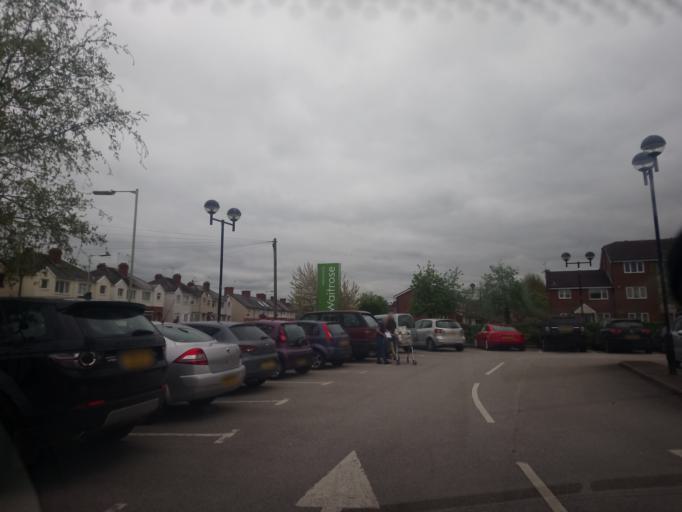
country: GB
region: England
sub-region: Telford and Wrekin
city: Newport
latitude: 52.7690
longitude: -2.3746
